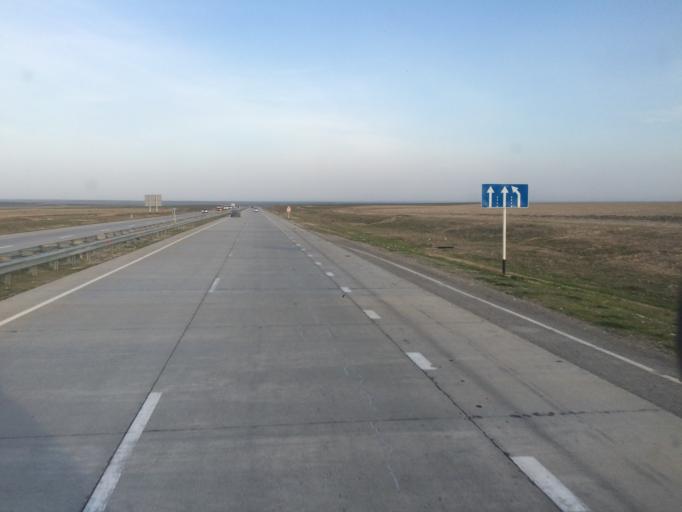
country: KZ
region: Ongtustik Qazaqstan
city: Temirlanovka
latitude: 42.6474
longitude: 69.2430
